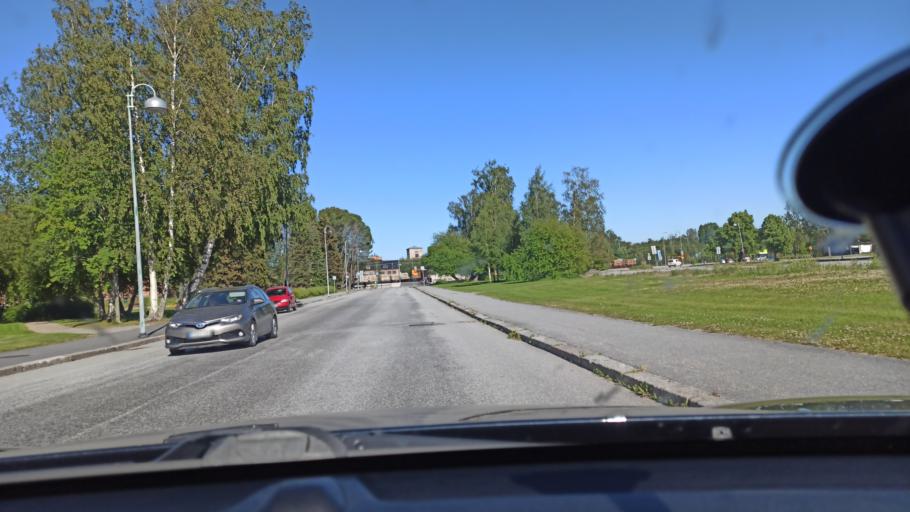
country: FI
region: Ostrobothnia
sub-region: Jakobstadsregionen
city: Jakobstad
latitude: 63.6747
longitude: 22.7090
